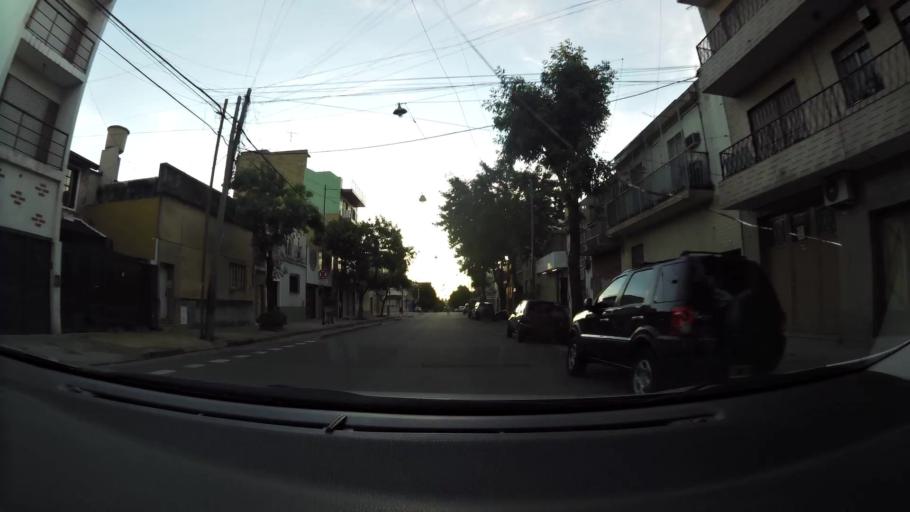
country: AR
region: Buenos Aires F.D.
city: Buenos Aires
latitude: -34.6386
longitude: -58.4271
